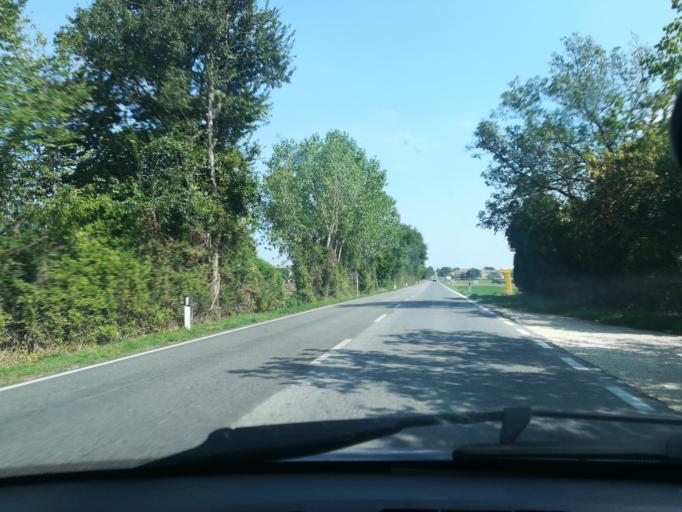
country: IT
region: The Marches
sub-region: Provincia di Macerata
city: Pollenza
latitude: 43.2350
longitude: 13.3580
